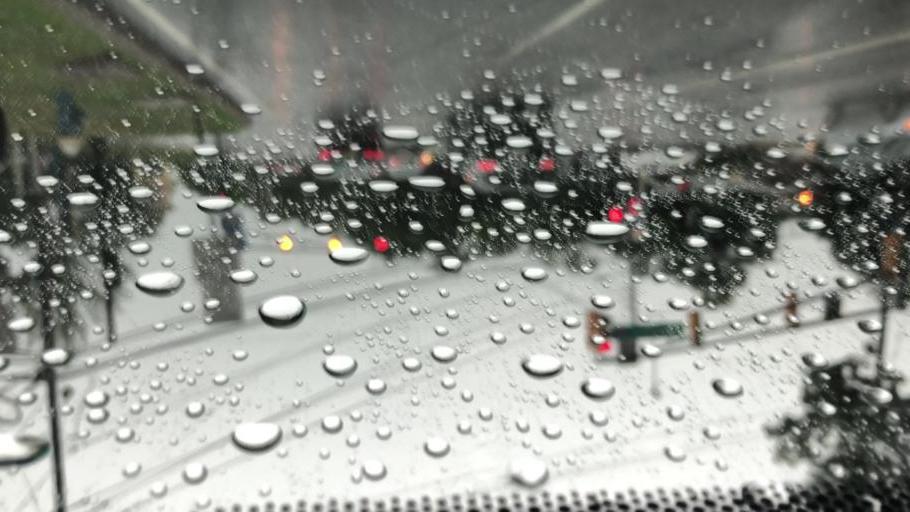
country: US
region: New Jersey
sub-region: Essex County
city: West Orange
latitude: 40.8033
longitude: -74.2476
